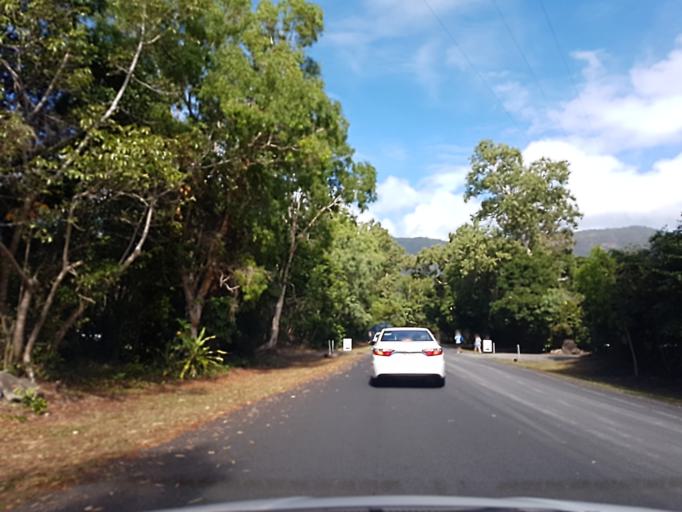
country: AU
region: Queensland
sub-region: Cairns
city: Palm Cove
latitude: -16.6622
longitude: 145.5656
